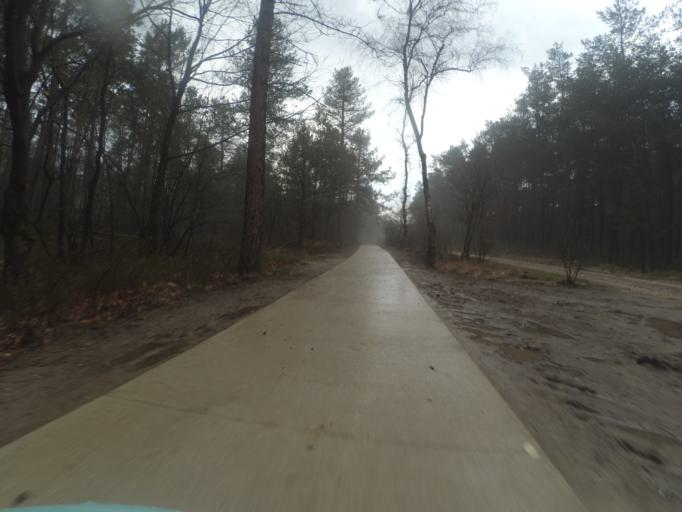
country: NL
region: Gelderland
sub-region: Gemeente Apeldoorn
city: Beekbergen
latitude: 52.1306
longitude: 5.9087
